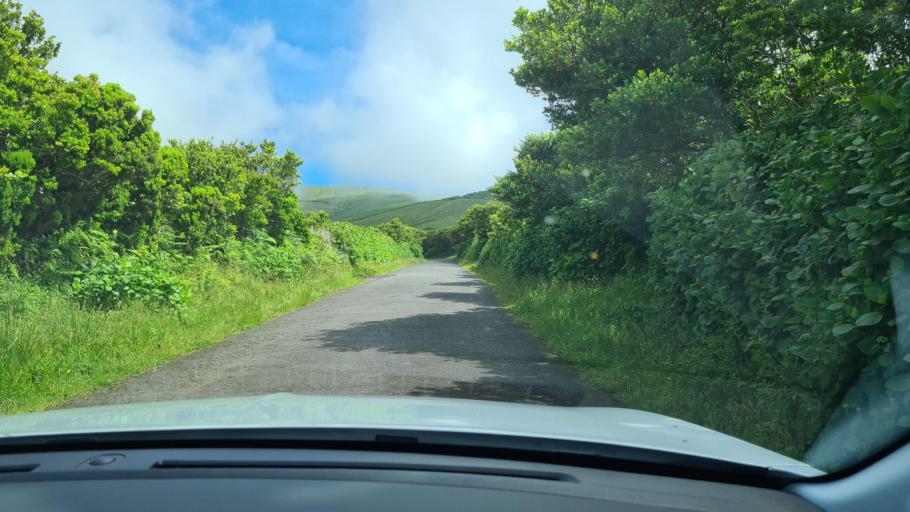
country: PT
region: Azores
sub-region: Sao Roque do Pico
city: Sao Roque do Pico
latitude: 38.6680
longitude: -28.1313
